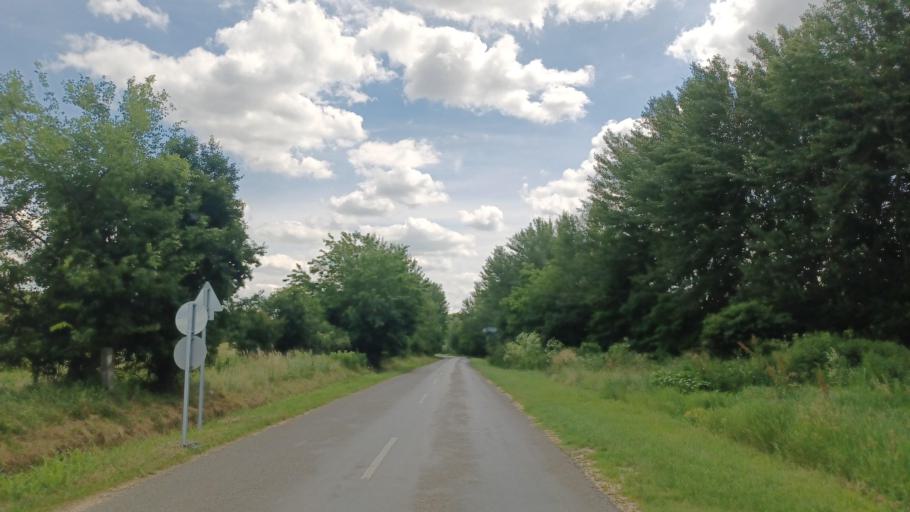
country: HU
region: Tolna
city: Simontornya
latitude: 46.7226
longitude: 18.4961
